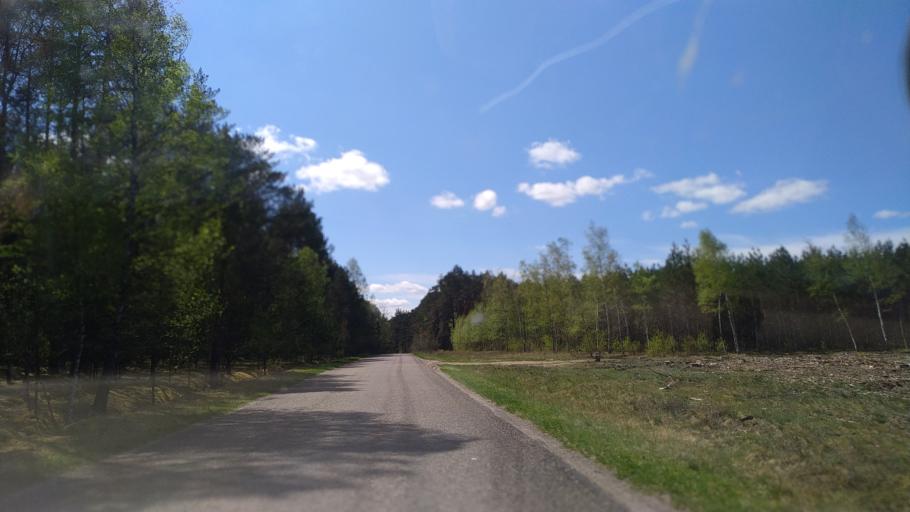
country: PL
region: Greater Poland Voivodeship
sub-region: Powiat pilski
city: Pila
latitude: 53.2600
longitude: 16.7579
